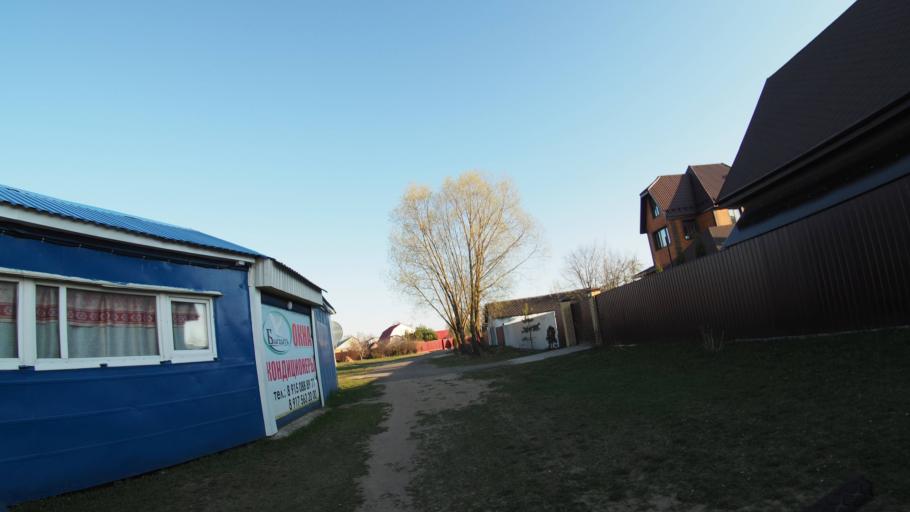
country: RU
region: Moskovskaya
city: Malyshevo
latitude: 55.4967
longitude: 38.3506
